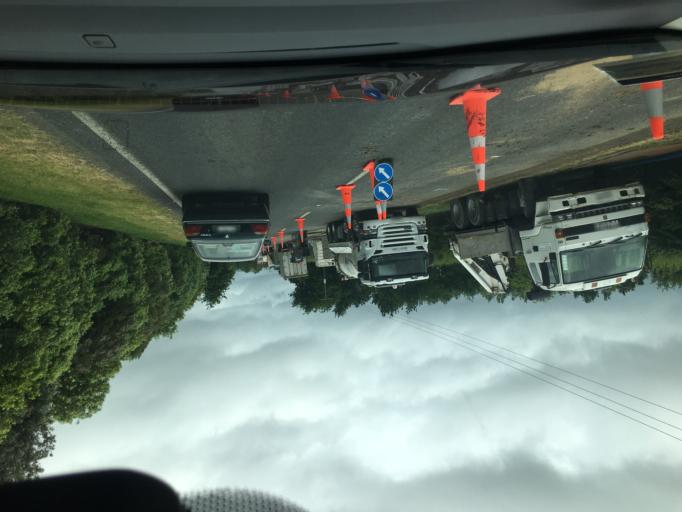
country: NZ
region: Waikato
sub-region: Waipa District
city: Cambridge
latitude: -37.9172
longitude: 175.4427
